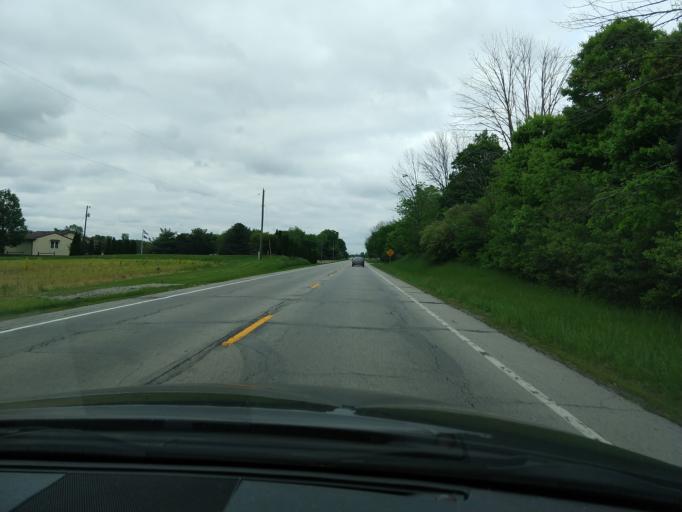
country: US
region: Indiana
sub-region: Madison County
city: Lapel
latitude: 40.0589
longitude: -85.8946
